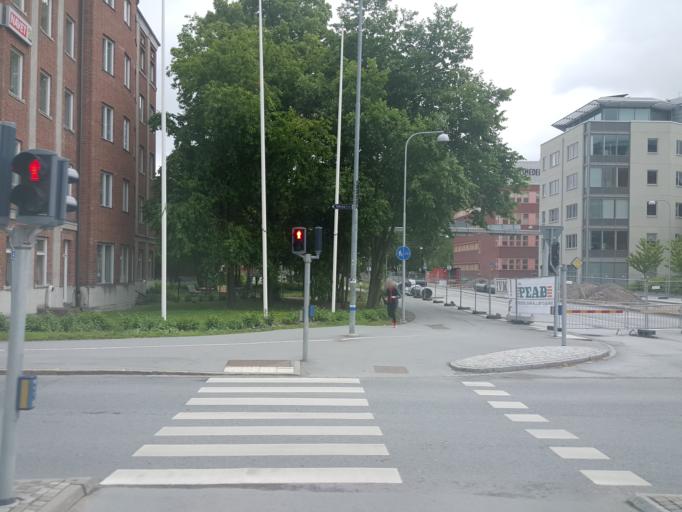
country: SE
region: Uppsala
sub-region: Uppsala Kommun
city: Uppsala
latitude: 59.8544
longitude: 17.6512
